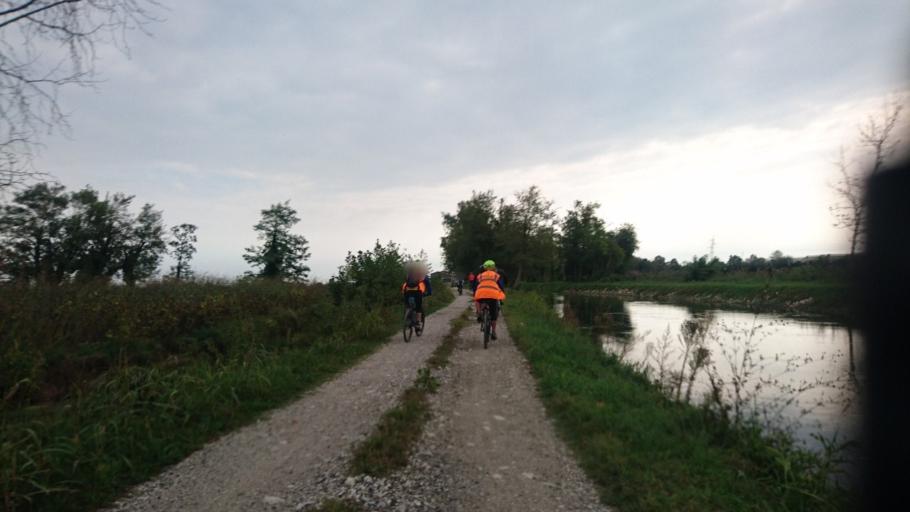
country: IT
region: Veneto
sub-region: Provincia di Verona
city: Monticelli-Fontana
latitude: 45.4028
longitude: 11.1283
